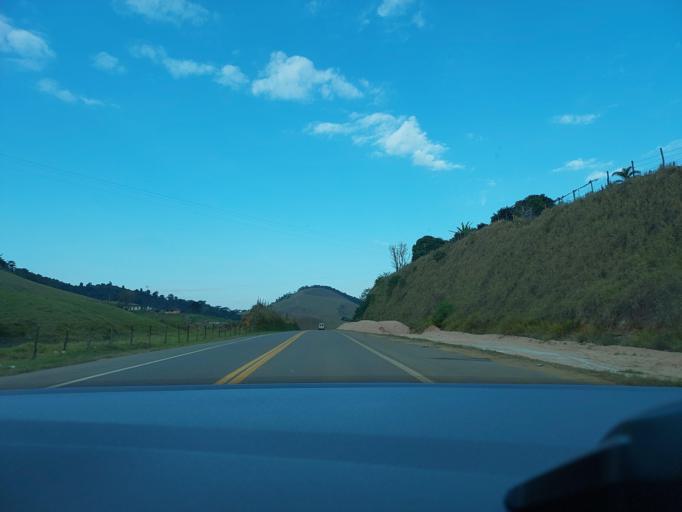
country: BR
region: Minas Gerais
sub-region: Muriae
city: Muriae
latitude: -21.0508
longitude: -42.5141
